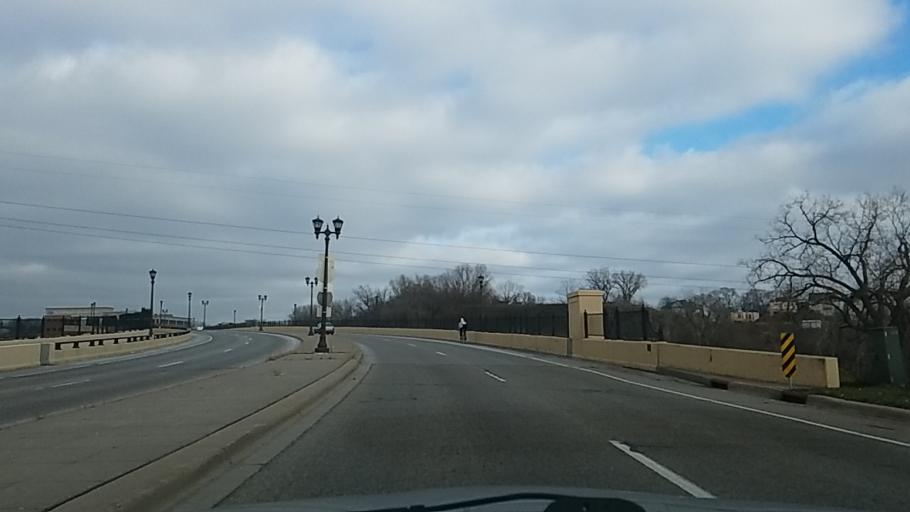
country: US
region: Minnesota
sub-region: Ramsey County
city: Saint Paul
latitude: 44.9615
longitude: -93.0873
